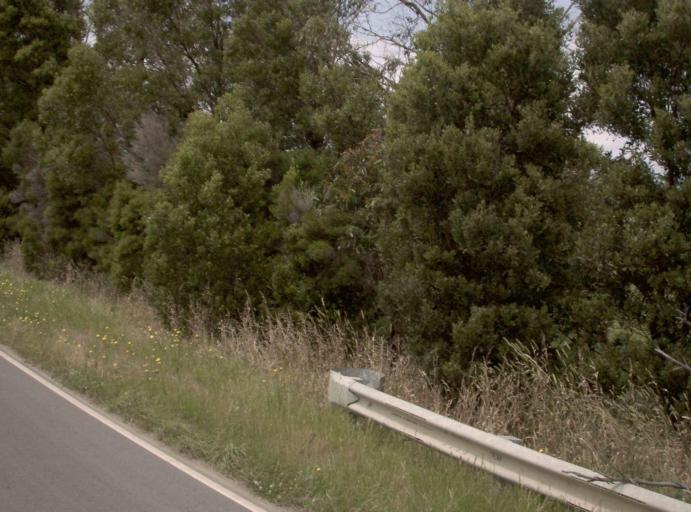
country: AU
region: Victoria
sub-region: Latrobe
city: Traralgon
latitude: -38.5038
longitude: 146.6661
